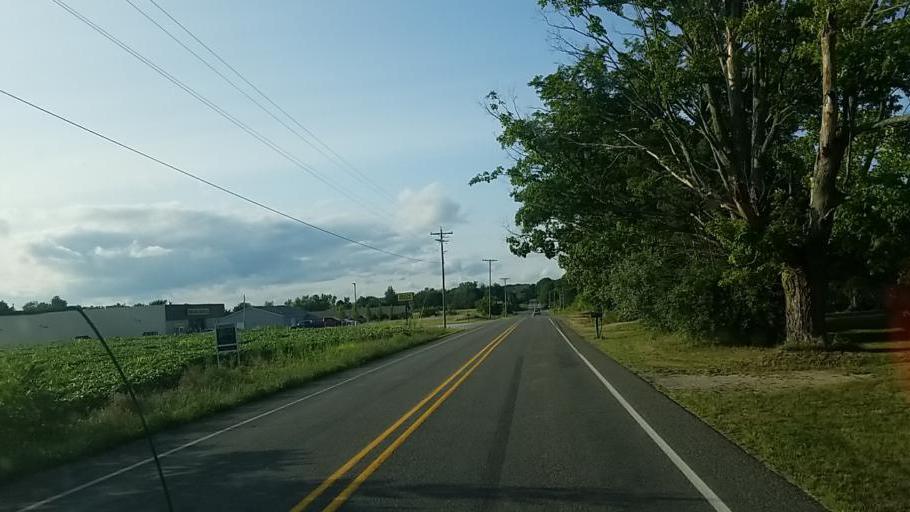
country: US
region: Michigan
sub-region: Montcalm County
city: Greenville
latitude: 43.2303
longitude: -85.3519
